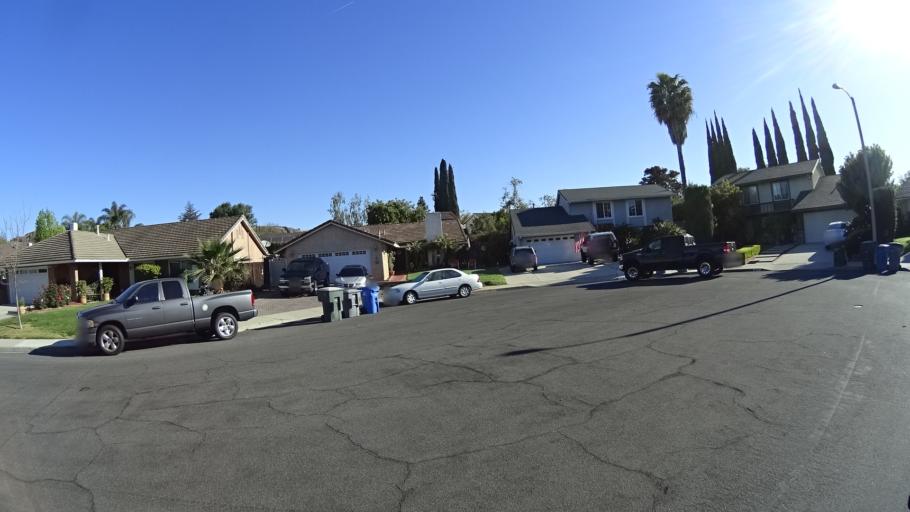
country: US
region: California
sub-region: Ventura County
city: Casa Conejo
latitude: 34.2143
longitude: -118.8996
